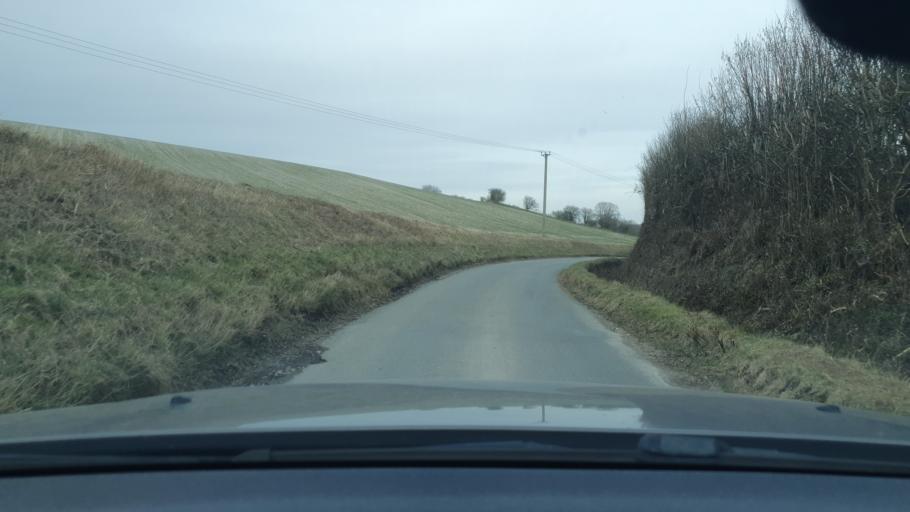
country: GB
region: England
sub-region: West Berkshire
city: Hungerford
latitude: 51.3703
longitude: -1.4917
